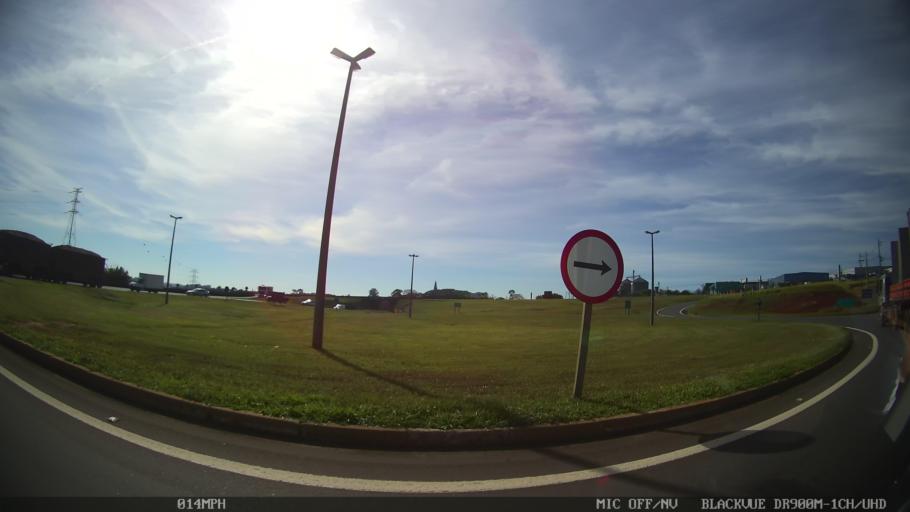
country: BR
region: Sao Paulo
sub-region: Araras
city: Araras
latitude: -22.3971
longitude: -47.3919
